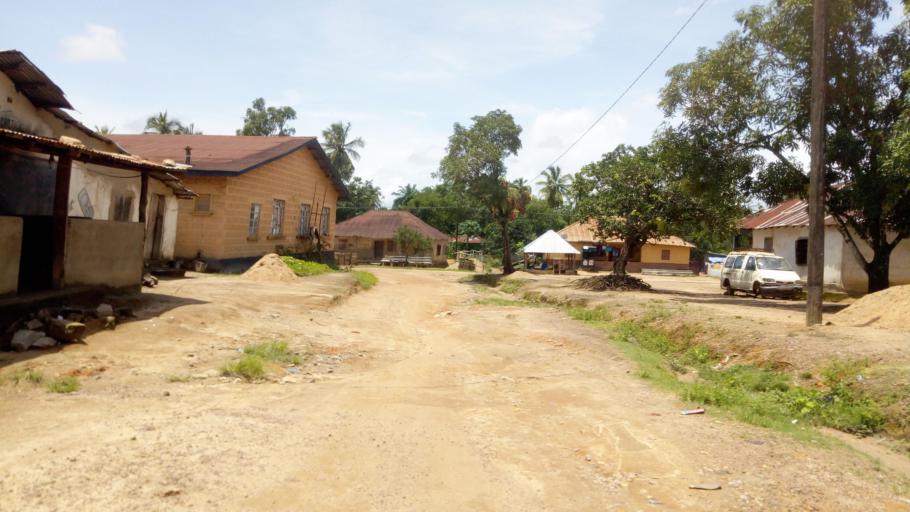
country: SL
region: Northern Province
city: Magburaka
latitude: 8.7164
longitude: -11.9592
